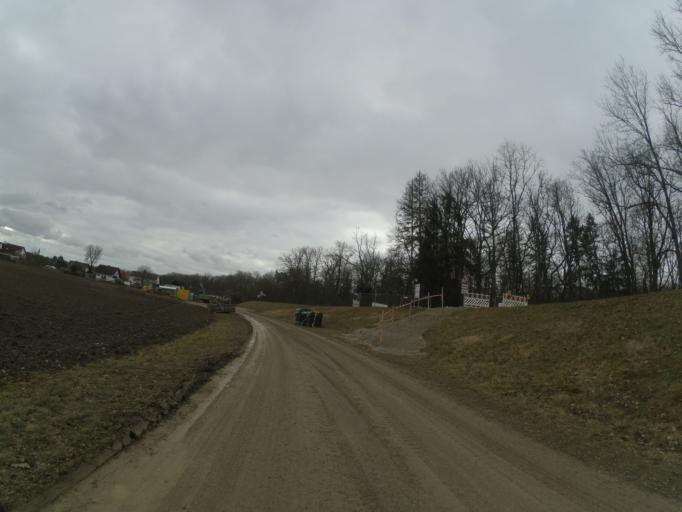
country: DE
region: Bavaria
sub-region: Swabia
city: Senden
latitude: 48.3005
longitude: 10.0480
